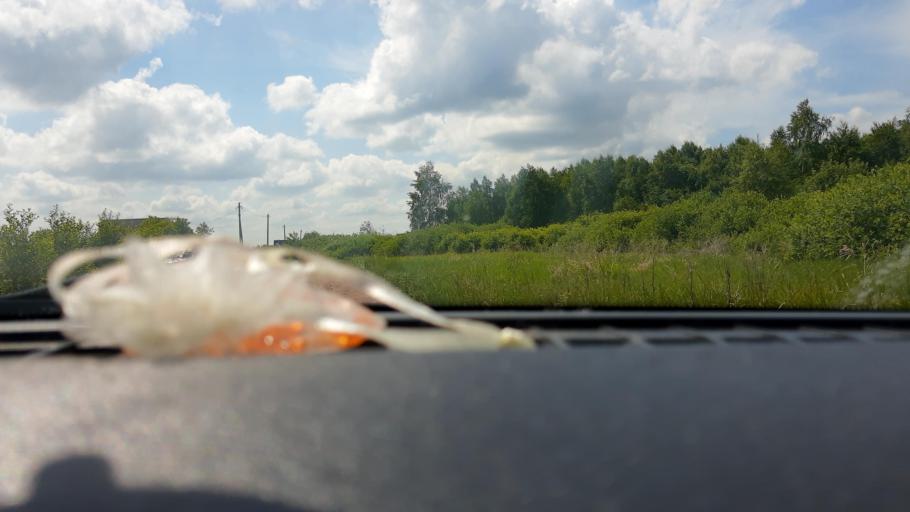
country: RU
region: Bashkortostan
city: Asanovo
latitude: 54.9190
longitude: 55.6324
